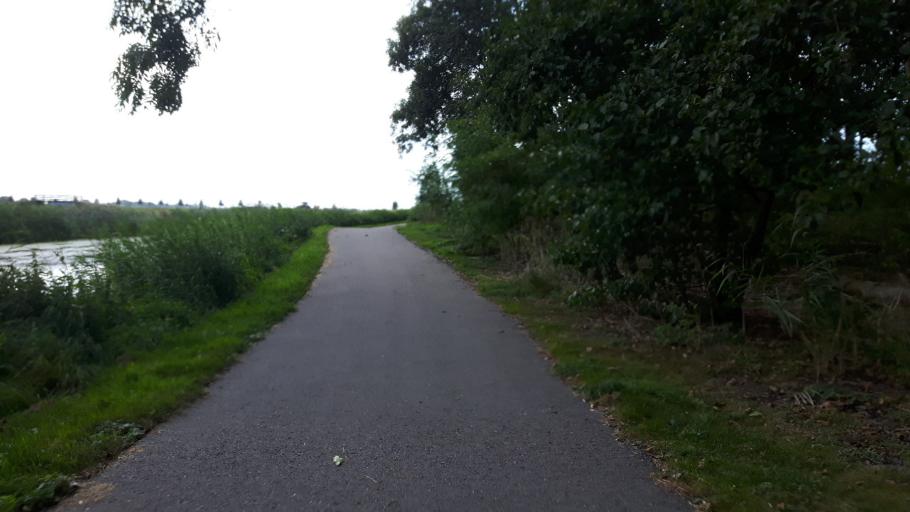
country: NL
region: North Holland
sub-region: Gemeente Medemblik
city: Opperdoes
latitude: 52.7139
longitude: 5.0972
